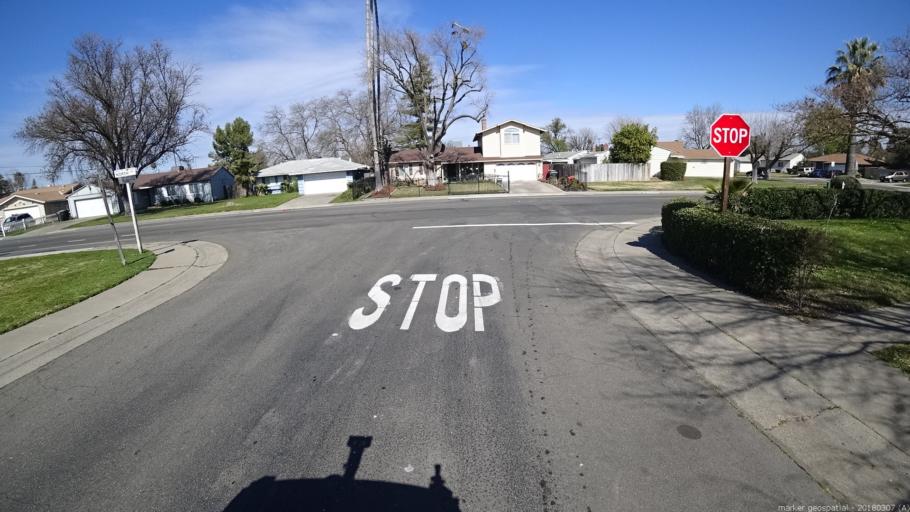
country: US
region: California
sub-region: Sacramento County
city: Parkway
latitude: 38.5021
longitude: -121.4429
